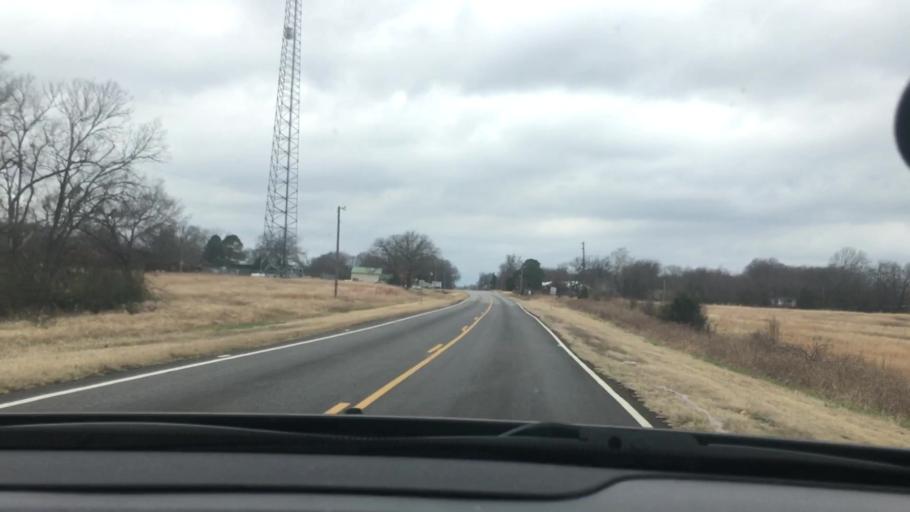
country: US
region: Oklahoma
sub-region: Coal County
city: Coalgate
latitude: 34.3750
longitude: -96.4132
